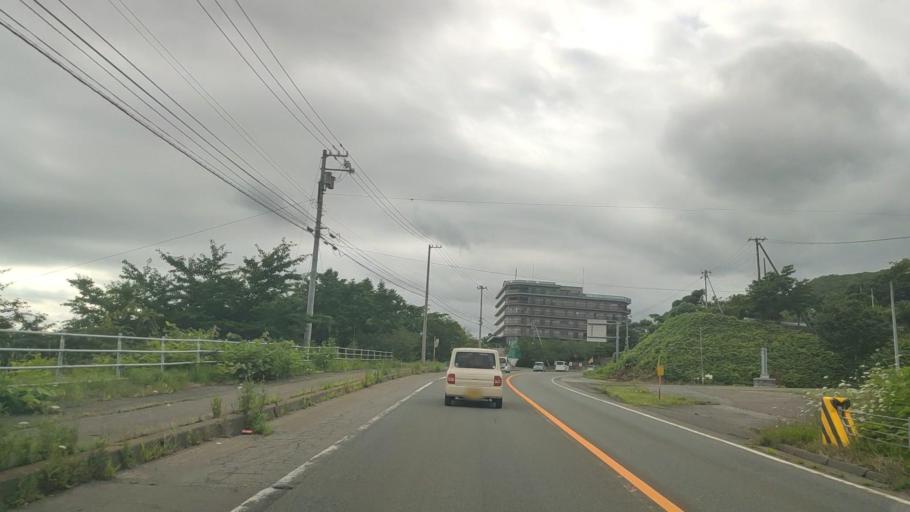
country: JP
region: Hokkaido
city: Date
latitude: 42.5575
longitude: 140.7488
